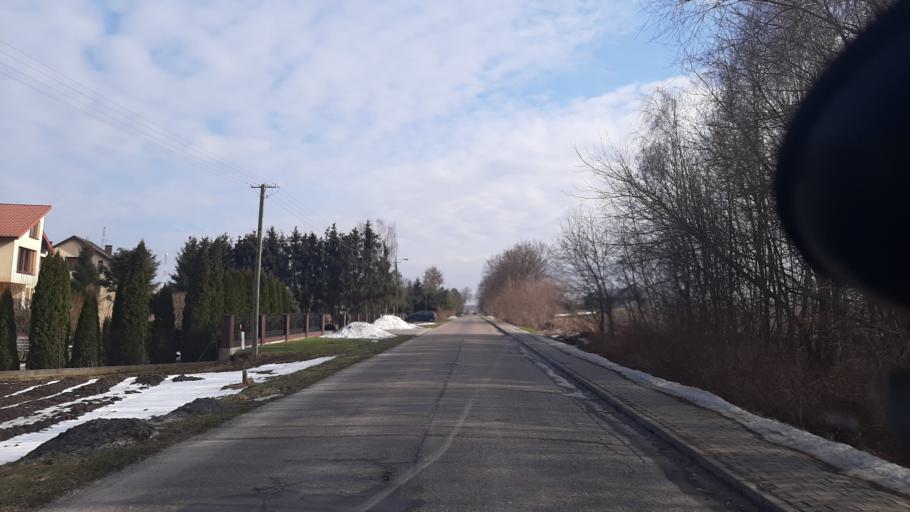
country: PL
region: Lublin Voivodeship
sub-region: Powiat lubartowski
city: Uscimow Stary
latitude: 51.4712
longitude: 22.9482
